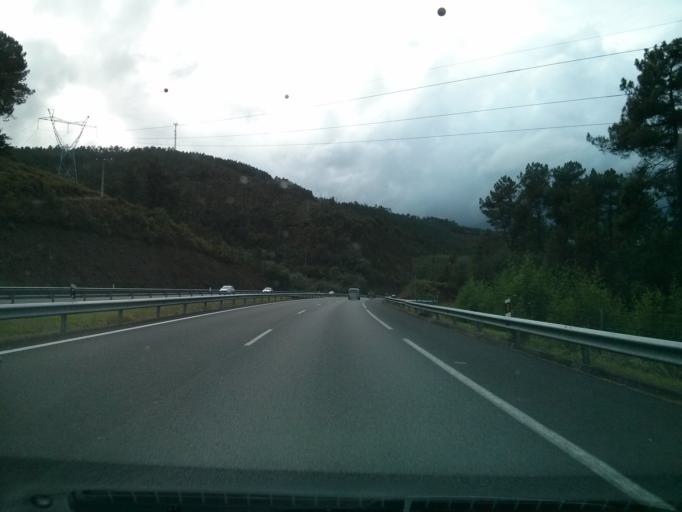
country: ES
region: Galicia
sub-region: Provincia de Ourense
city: Toen
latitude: 42.3343
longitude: -7.9770
